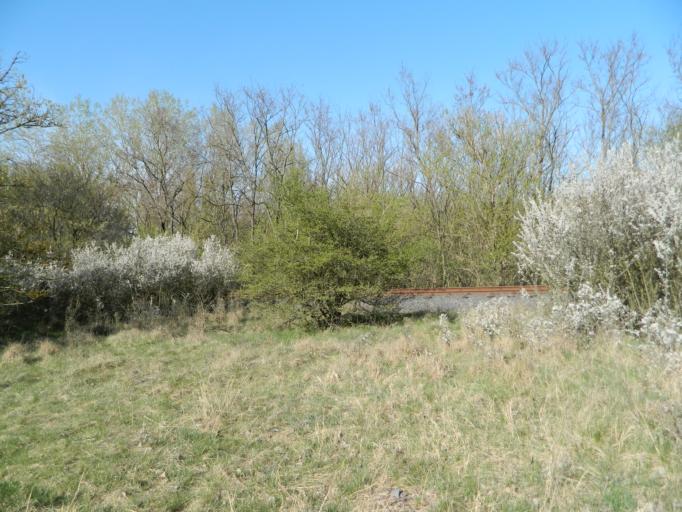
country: HU
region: Fejer
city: Pakozd
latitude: 47.2105
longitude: 18.4967
